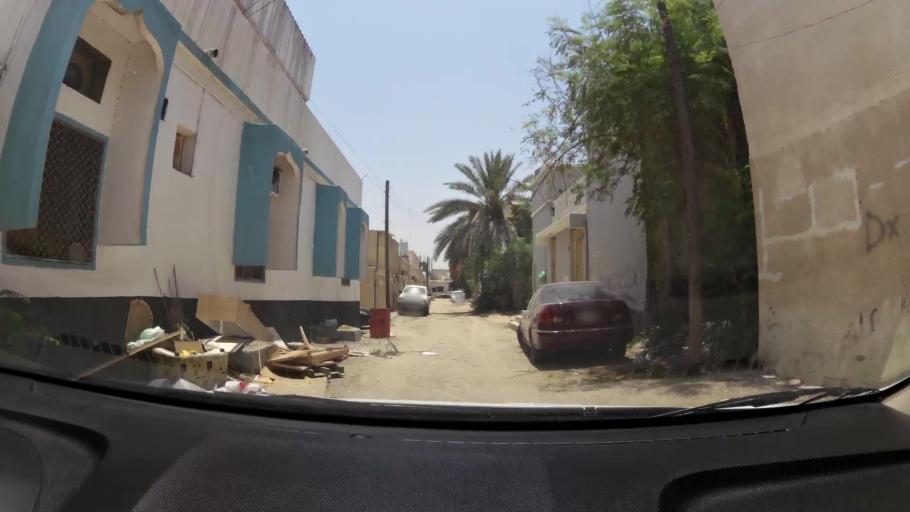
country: AE
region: Ajman
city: Ajman
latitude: 25.3982
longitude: 55.4392
